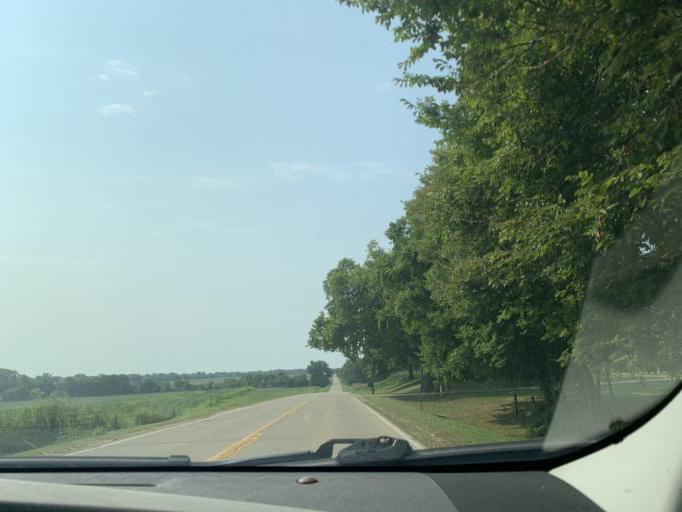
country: US
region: Illinois
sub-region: Whiteside County
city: Sterling
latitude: 41.8110
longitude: -89.7422
